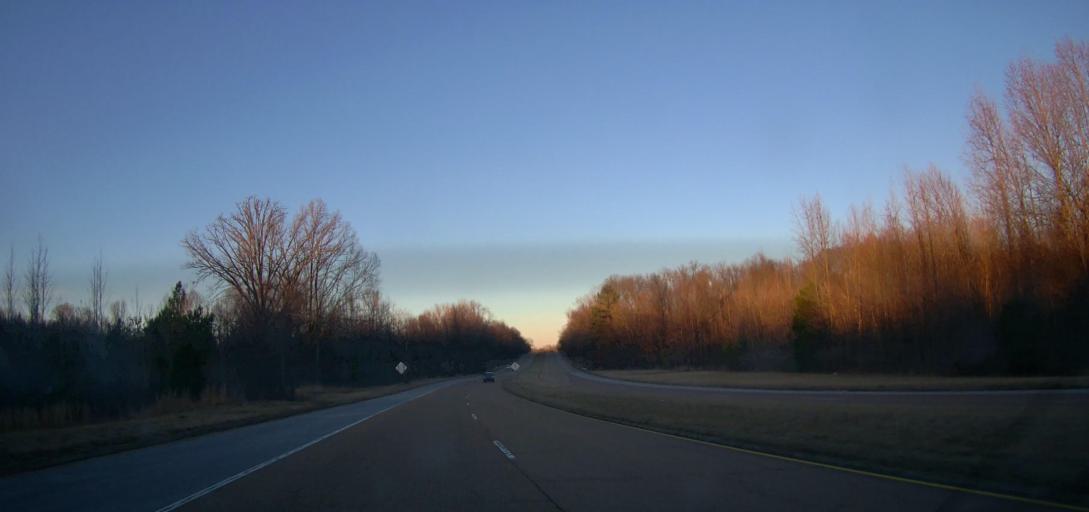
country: US
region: Tennessee
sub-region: Shelby County
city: Bartlett
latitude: 35.2447
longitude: -89.8972
